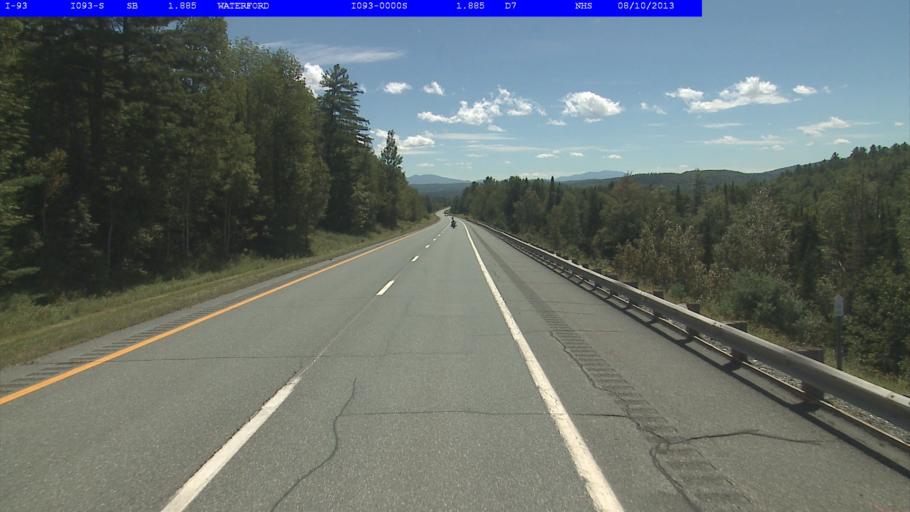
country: US
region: Vermont
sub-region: Caledonia County
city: Saint Johnsbury
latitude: 44.3687
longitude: -71.9047
